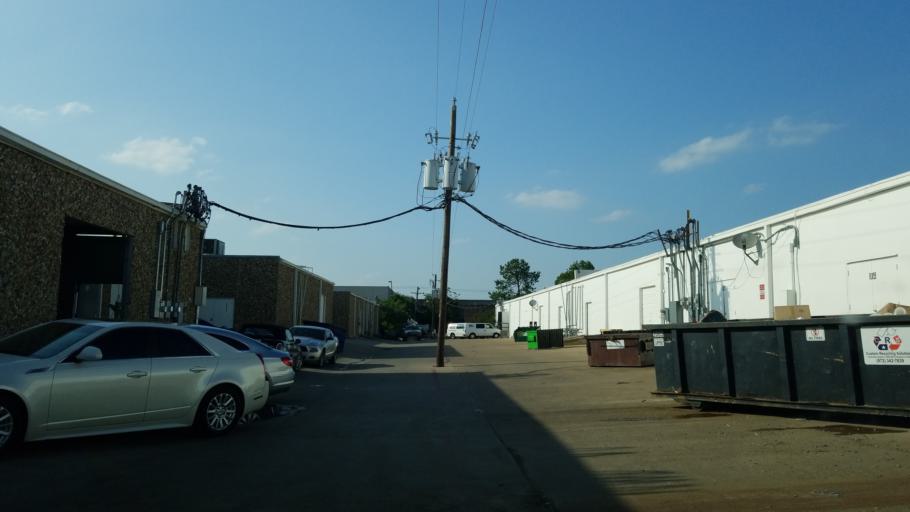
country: US
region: Texas
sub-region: Dallas County
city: Farmers Branch
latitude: 32.8727
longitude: -96.8938
